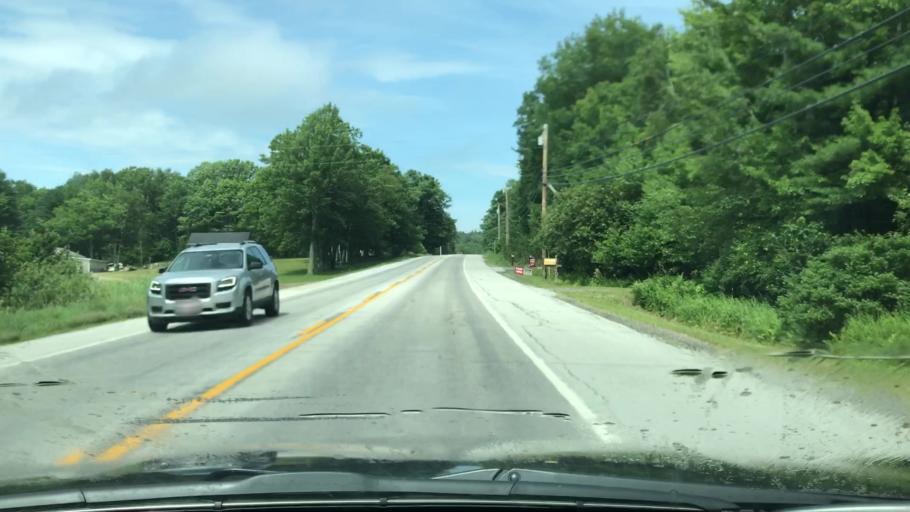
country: US
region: Maine
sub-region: Waldo County
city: Northport
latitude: 44.3482
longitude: -68.9692
